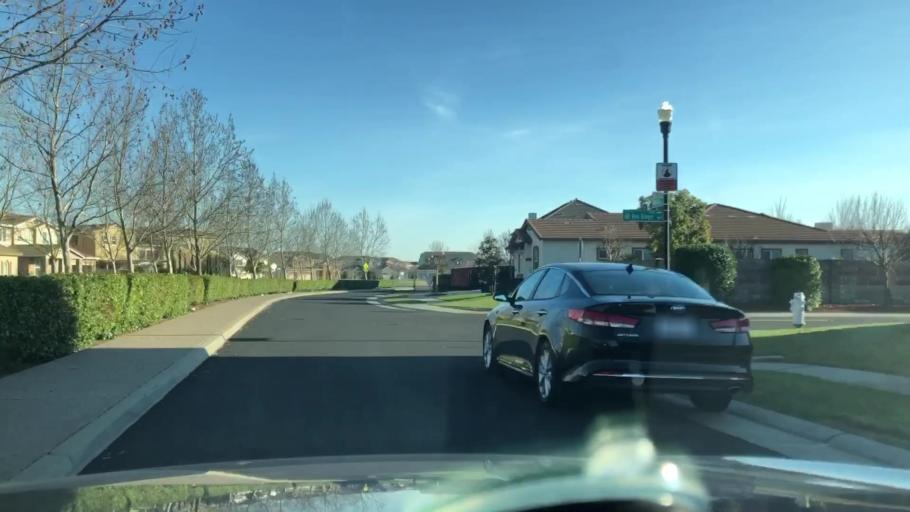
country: US
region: California
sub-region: Sacramento County
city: Laguna
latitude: 38.3985
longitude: -121.4043
